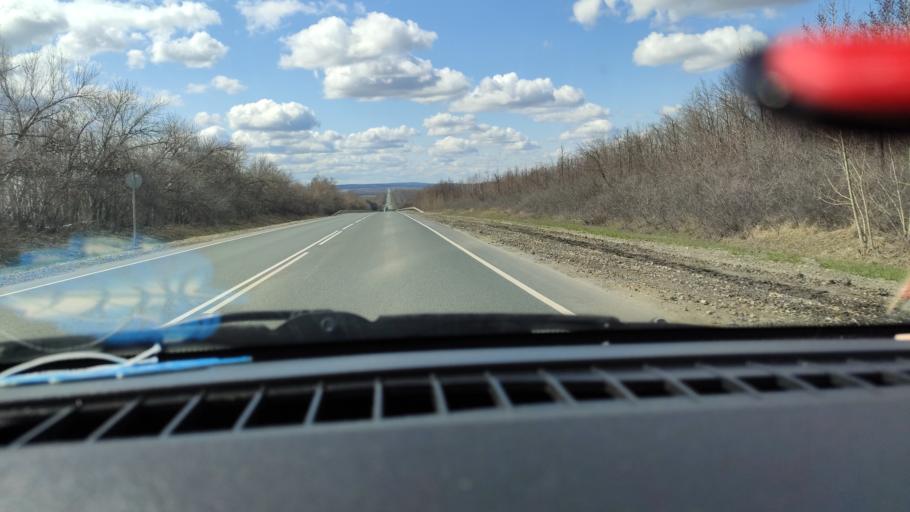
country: RU
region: Saratov
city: Khvalynsk
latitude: 52.6162
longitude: 48.1666
